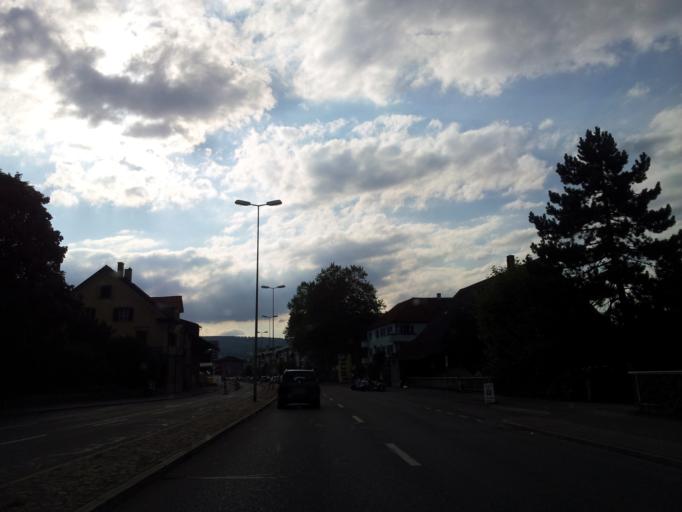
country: CH
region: Zurich
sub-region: Bezirk Dietikon
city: Schlieren / Zentrum
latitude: 47.3975
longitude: 8.4464
